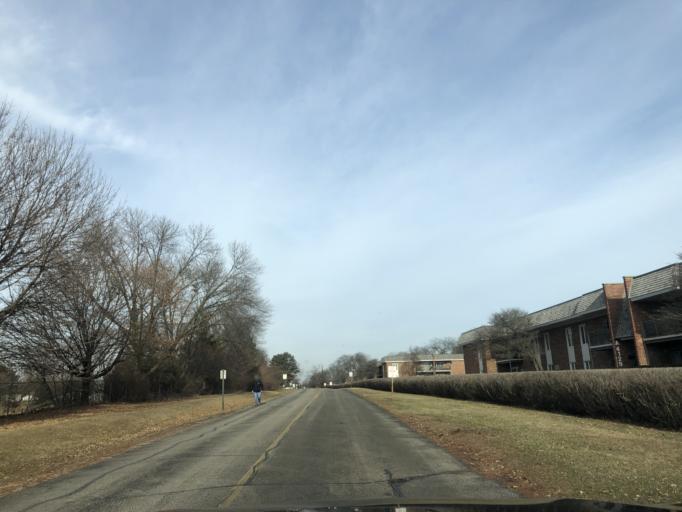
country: US
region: Illinois
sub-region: DuPage County
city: Downers Grove
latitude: 41.8113
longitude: -88.0148
